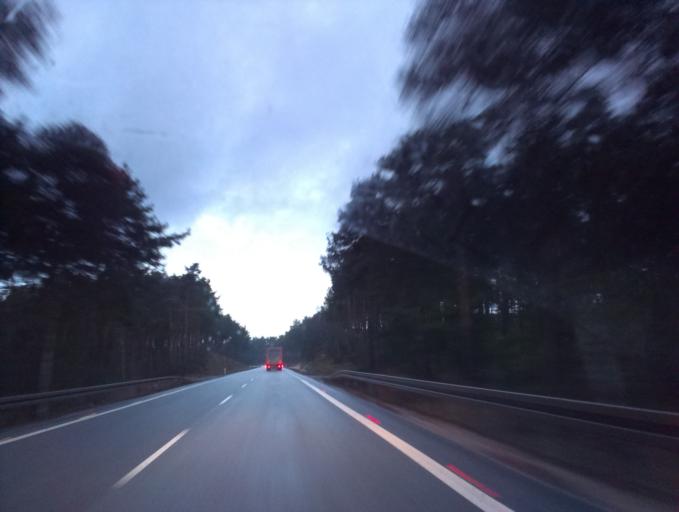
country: PL
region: Swietokrzyskie
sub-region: Powiat konecki
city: Ruda Maleniecka
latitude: 51.1802
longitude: 20.2198
